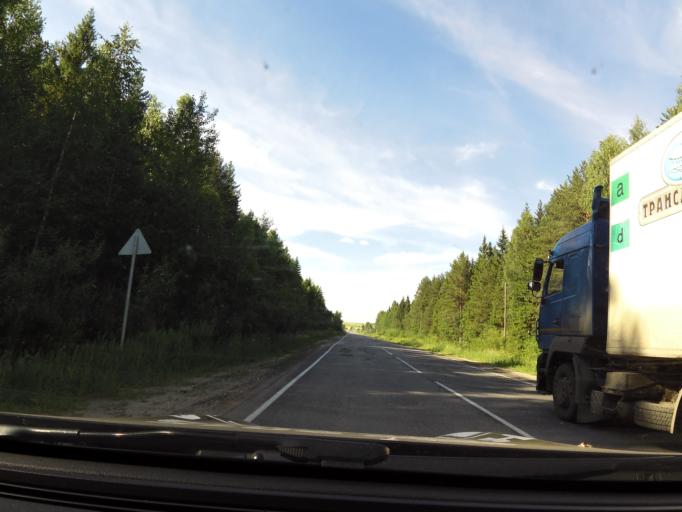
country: RU
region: Kirov
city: Belaya Kholunitsa
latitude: 58.8830
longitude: 50.8726
